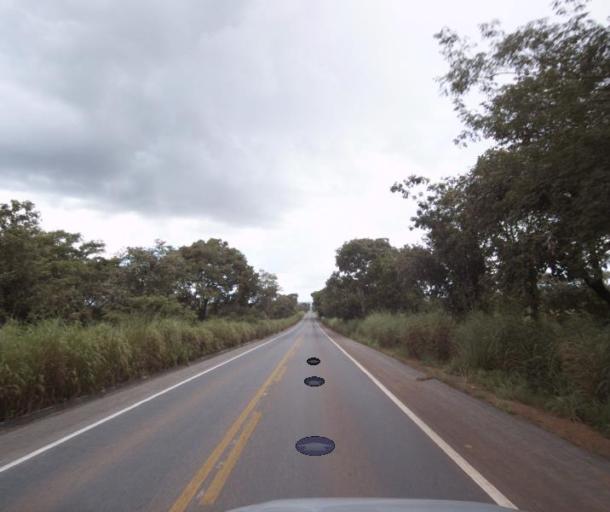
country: BR
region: Goias
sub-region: Porangatu
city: Porangatu
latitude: -13.3224
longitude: -49.1189
